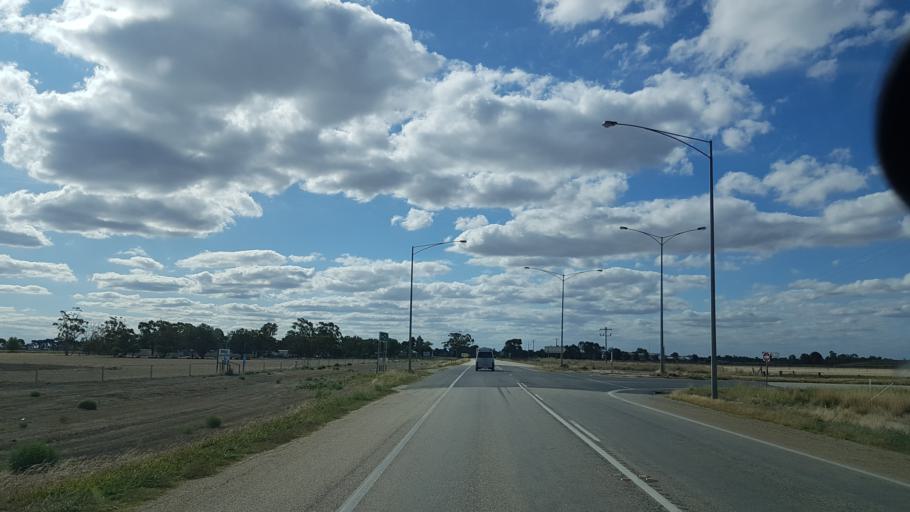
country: AU
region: Victoria
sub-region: Swan Hill
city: Swan Hill
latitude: -35.7636
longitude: 143.9314
